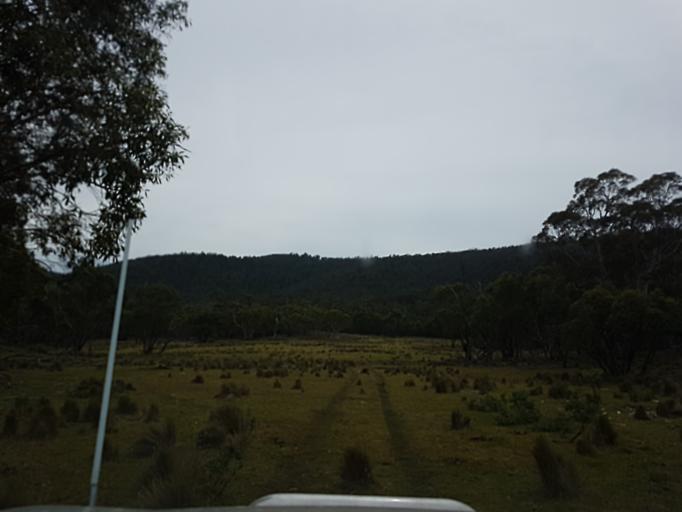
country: AU
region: New South Wales
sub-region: Snowy River
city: Jindabyne
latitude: -36.8575
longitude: 148.2656
